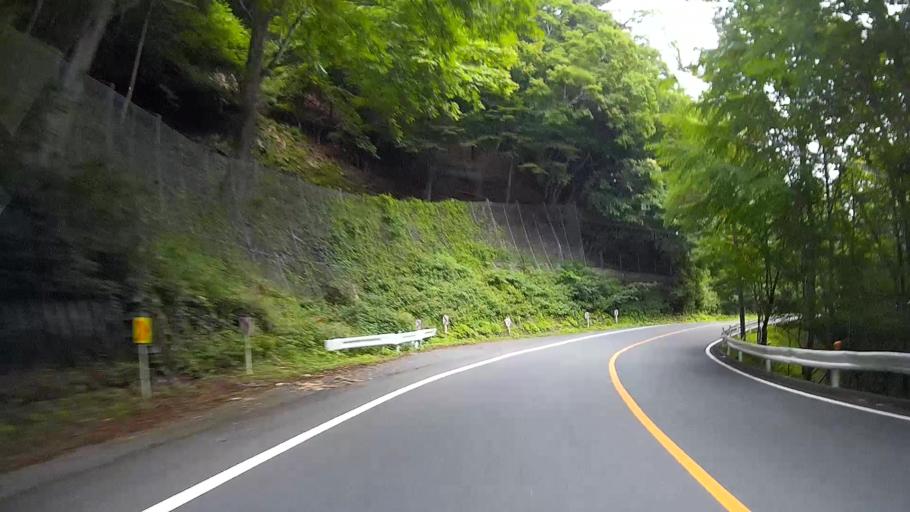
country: JP
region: Yamanashi
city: Enzan
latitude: 35.9184
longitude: 138.8306
